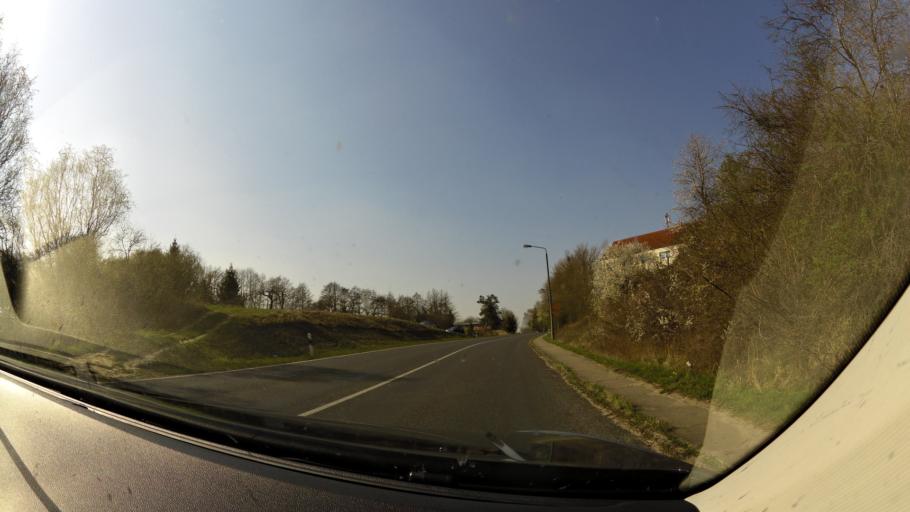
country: DE
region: Mecklenburg-Vorpommern
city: Bad Sulze
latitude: 54.1084
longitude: 12.6505
